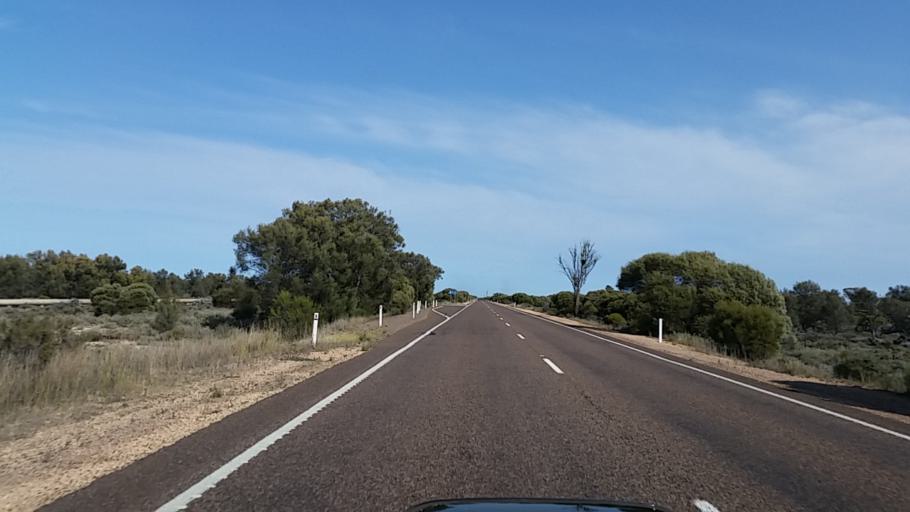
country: AU
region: South Australia
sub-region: Whyalla
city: Whyalla
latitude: -32.9135
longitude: 137.5656
